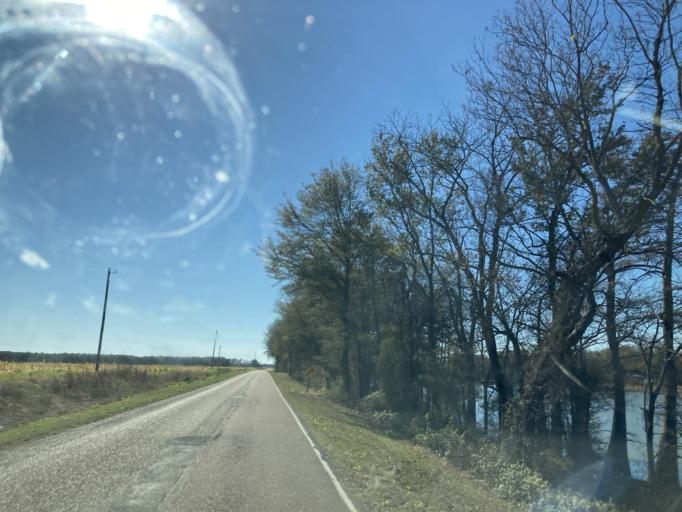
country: US
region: Mississippi
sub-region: Yazoo County
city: Yazoo City
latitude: 32.9212
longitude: -90.4944
